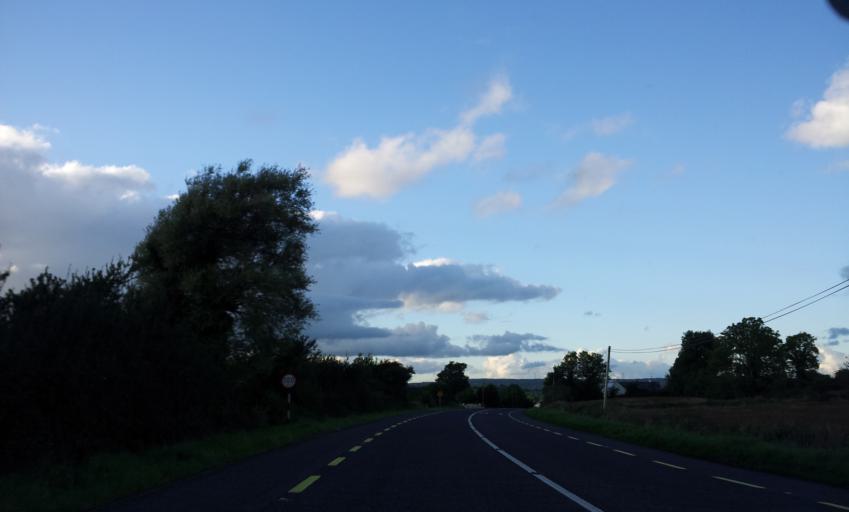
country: IE
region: Munster
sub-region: County Limerick
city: Abbeyfeale
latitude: 52.3616
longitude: -9.3251
